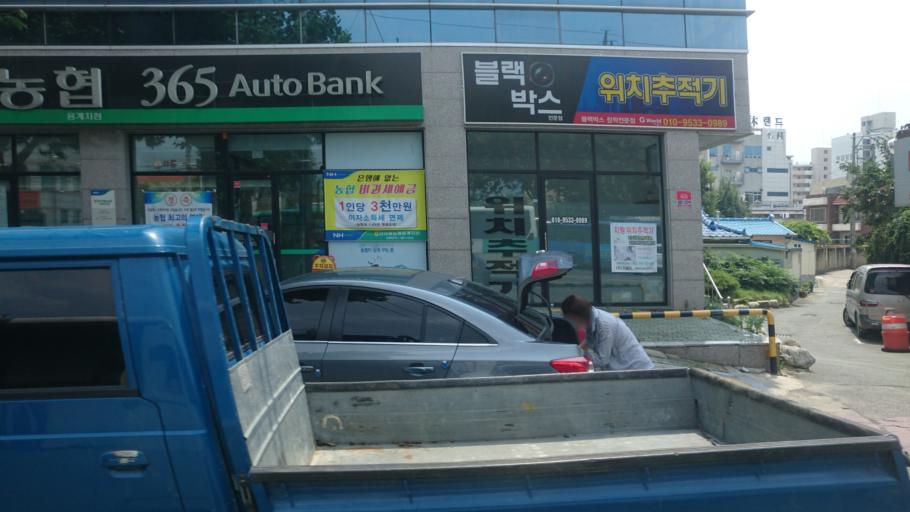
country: KR
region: Gyeongsangbuk-do
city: Gyeongsan-si
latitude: 35.8780
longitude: 128.6757
